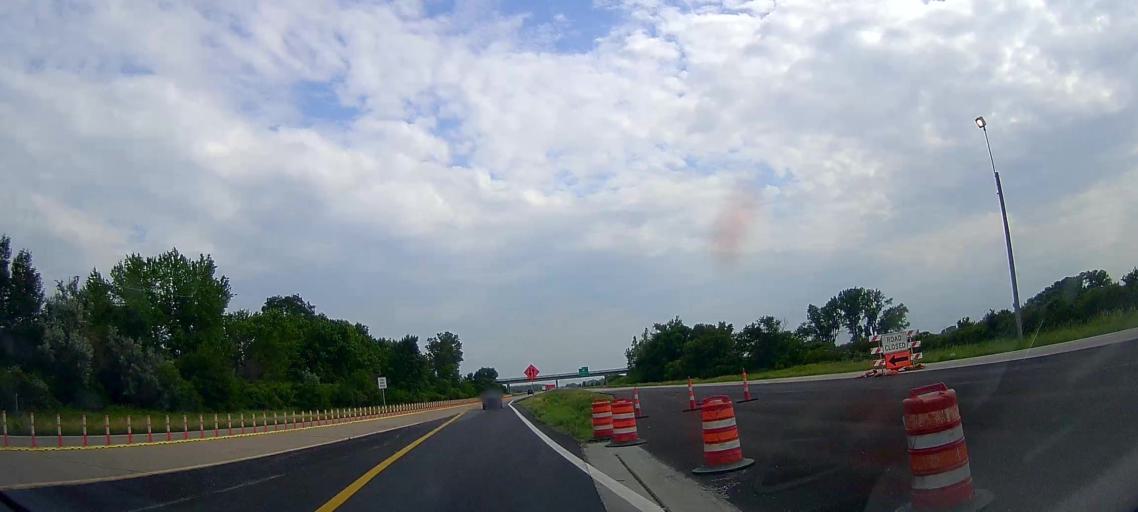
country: US
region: Nebraska
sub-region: Burt County
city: Tekamah
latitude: 41.7315
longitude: -96.0478
